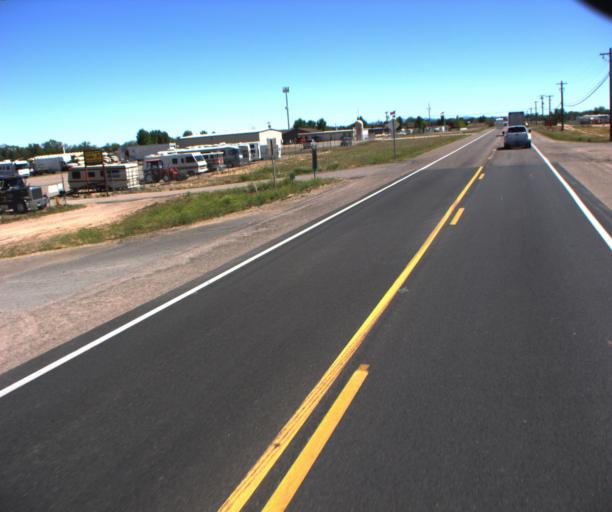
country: US
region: Arizona
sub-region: Yavapai County
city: Chino Valley
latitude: 34.7865
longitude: -112.4522
